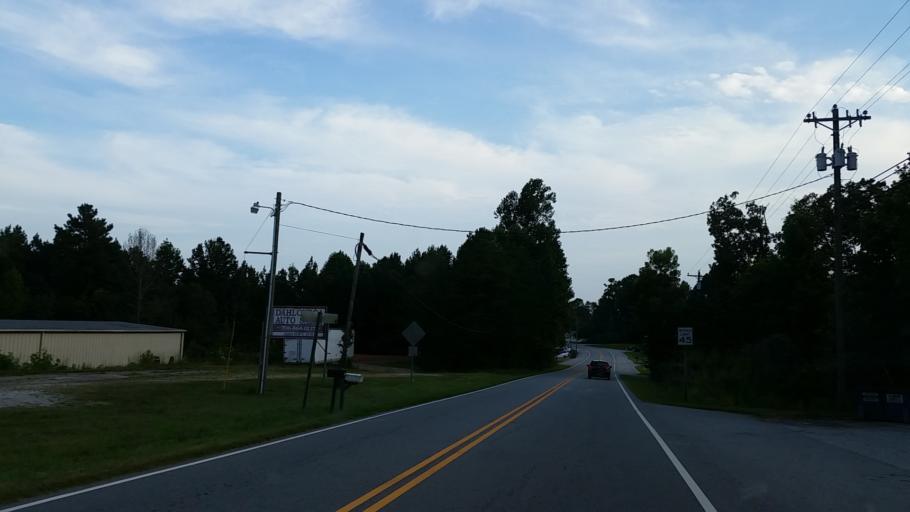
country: US
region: Georgia
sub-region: Lumpkin County
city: Dahlonega
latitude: 34.5605
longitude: -83.9972
